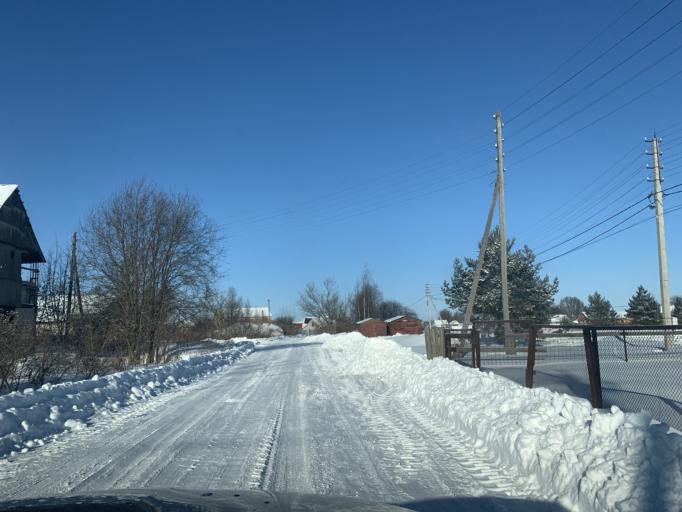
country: RU
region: Jaroslavl
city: Tunoshna
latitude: 57.6610
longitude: 40.0679
